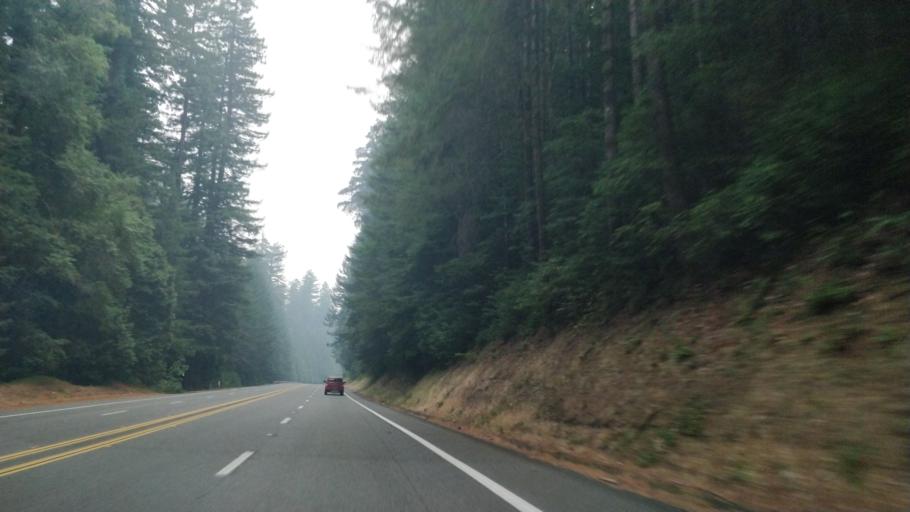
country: US
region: California
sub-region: Humboldt County
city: Rio Dell
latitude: 40.3694
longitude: -123.9259
